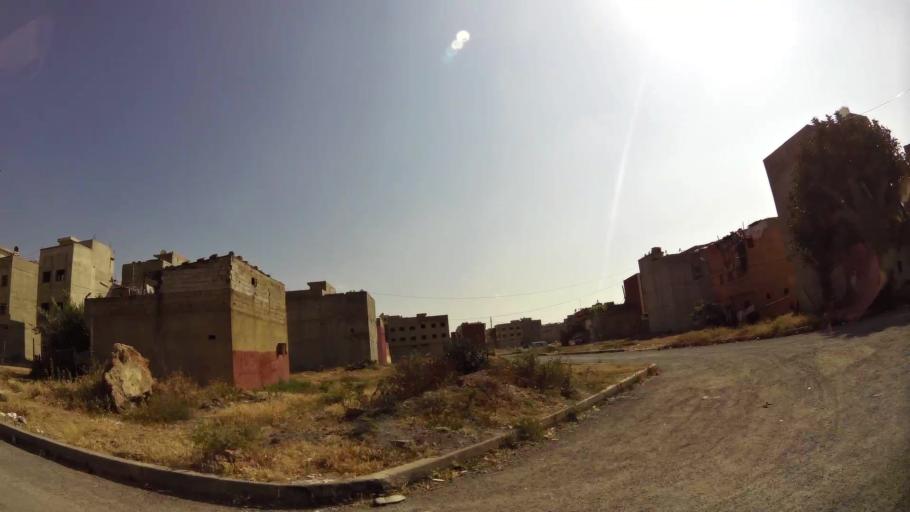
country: MA
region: Rabat-Sale-Zemmour-Zaer
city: Sale
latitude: 34.0636
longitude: -6.7663
